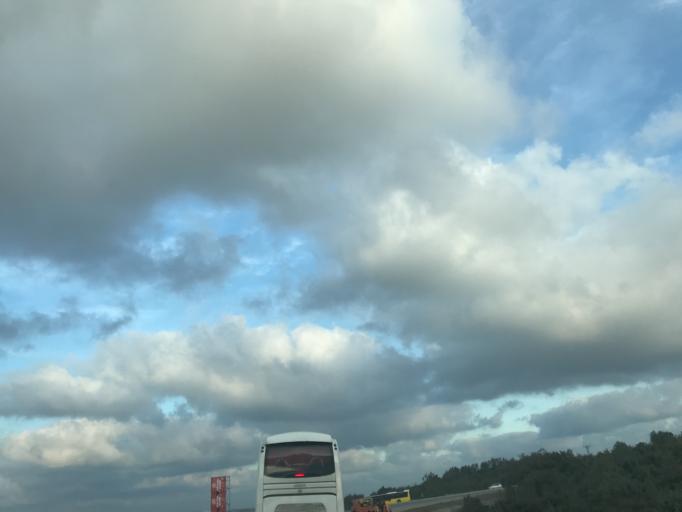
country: TR
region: Istanbul
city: Durusu
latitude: 41.2632
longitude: 28.6980
